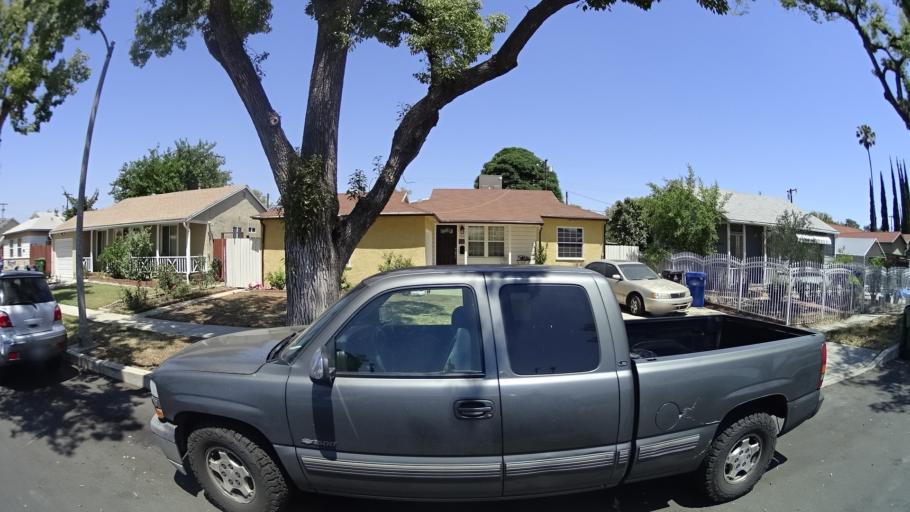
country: US
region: California
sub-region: Los Angeles County
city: Van Nuys
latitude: 34.2154
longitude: -118.4390
